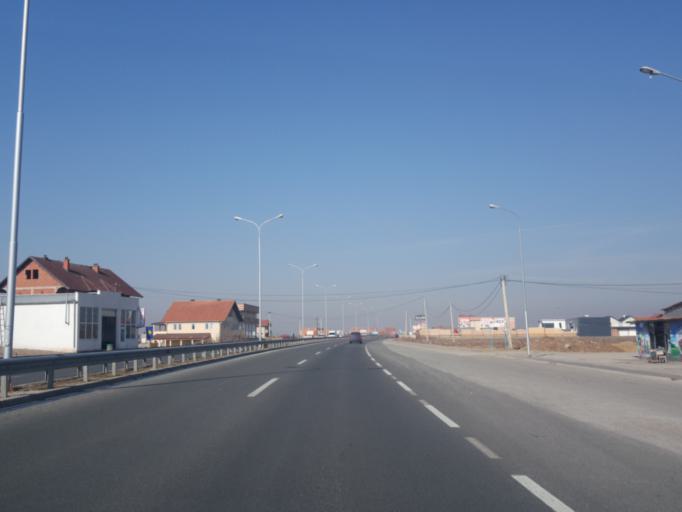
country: XK
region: Pristina
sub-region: Komuna e Obiliqit
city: Obiliq
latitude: 42.7407
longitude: 21.0520
